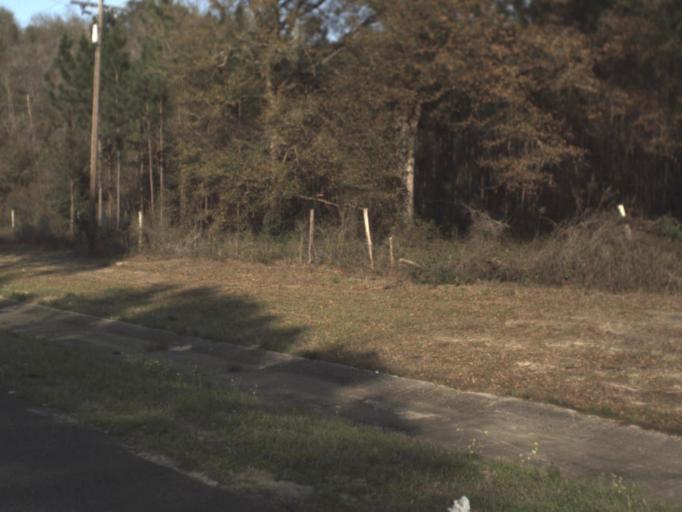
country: US
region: Florida
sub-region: Calhoun County
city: Blountstown
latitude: 30.5372
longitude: -85.1915
